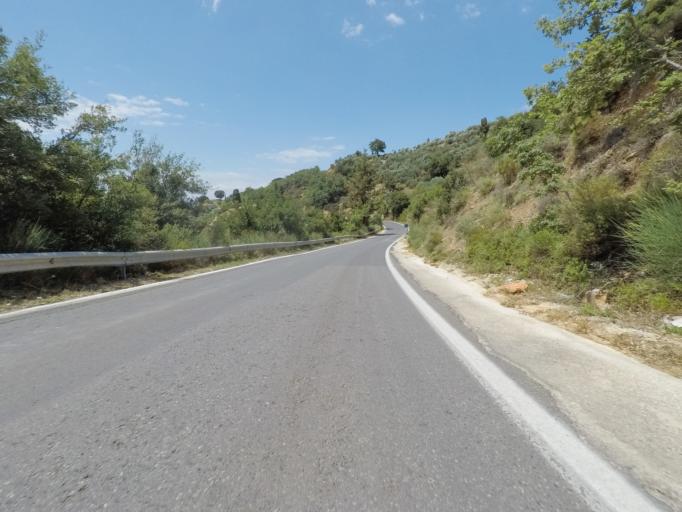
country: GR
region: Crete
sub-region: Nomos Irakleiou
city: Mokhos
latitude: 35.2259
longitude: 25.4624
